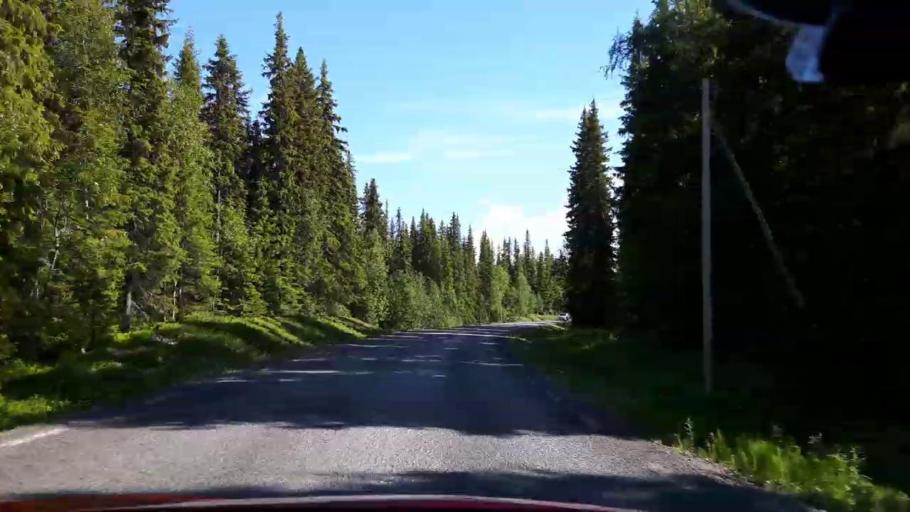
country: SE
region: Jaemtland
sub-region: Krokoms Kommun
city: Valla
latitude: 63.7375
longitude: 14.1191
